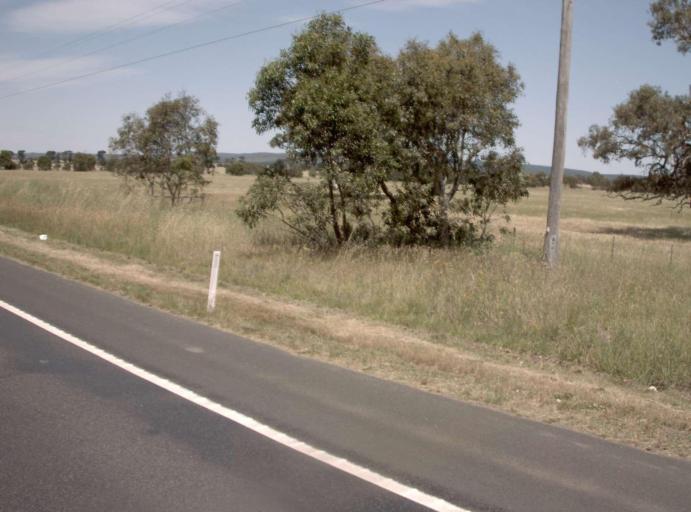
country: AU
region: Victoria
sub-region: Wellington
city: Heyfield
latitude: -38.1590
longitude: 146.7274
